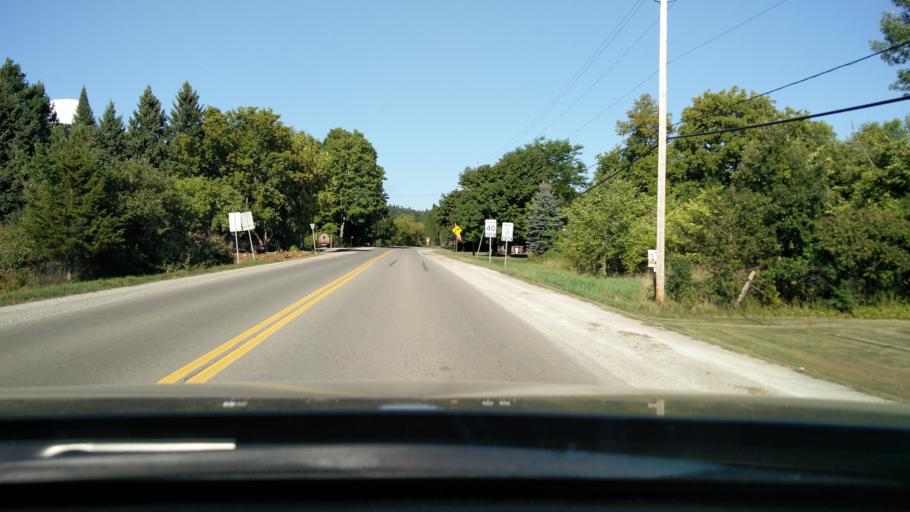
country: CA
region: Ontario
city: Perth
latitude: 44.6792
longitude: -76.4105
